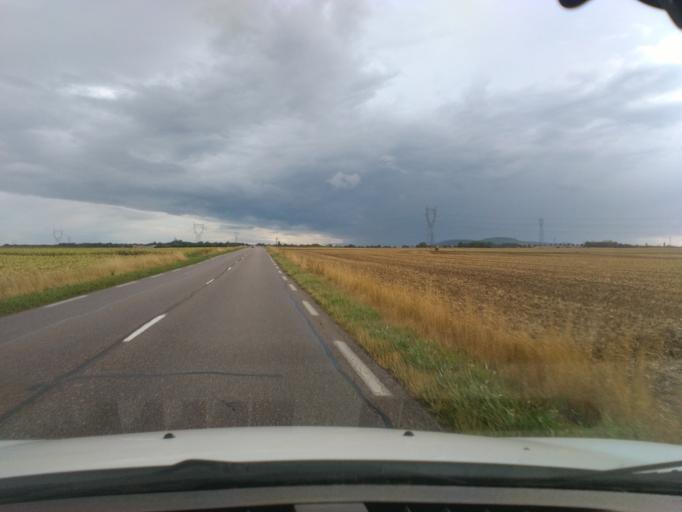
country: FR
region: Lorraine
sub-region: Departement de Meurthe-et-Moselle
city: Vezelise
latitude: 48.4871
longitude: 6.1441
